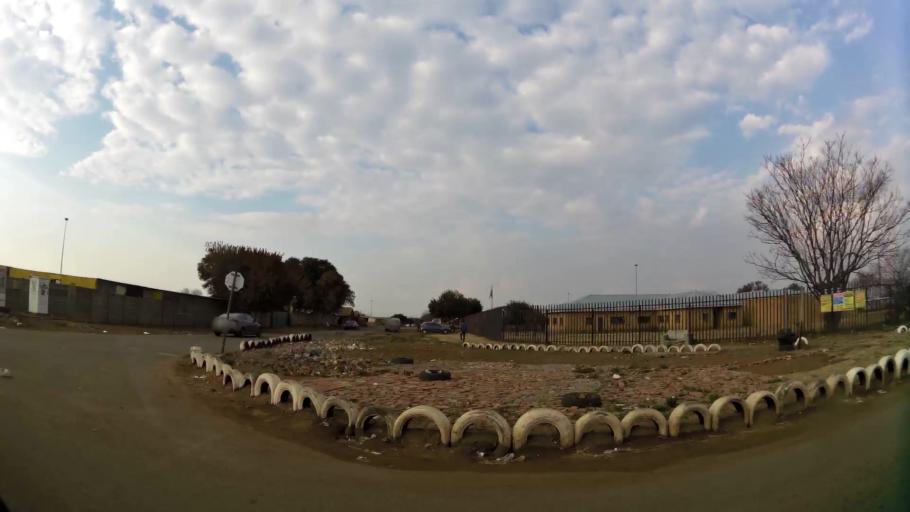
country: ZA
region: Gauteng
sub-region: Sedibeng District Municipality
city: Vanderbijlpark
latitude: -26.6814
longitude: 27.8768
